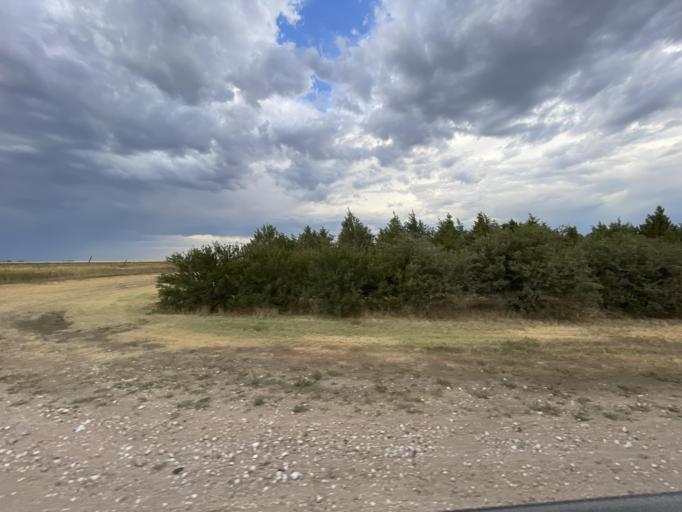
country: US
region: Nebraska
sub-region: Red Willow County
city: McCook
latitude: 40.2535
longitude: -100.7598
